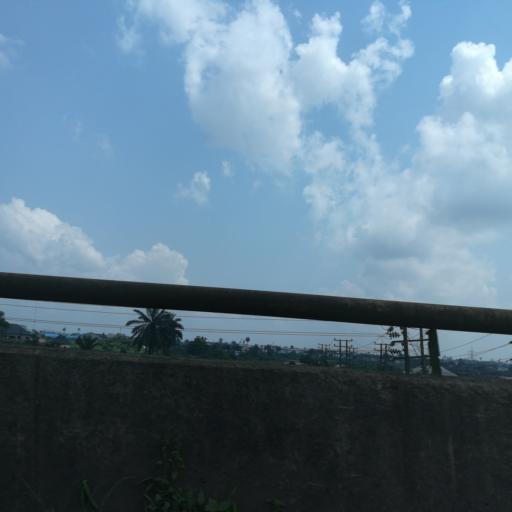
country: NG
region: Rivers
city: Port Harcourt
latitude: 4.8439
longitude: 7.0784
